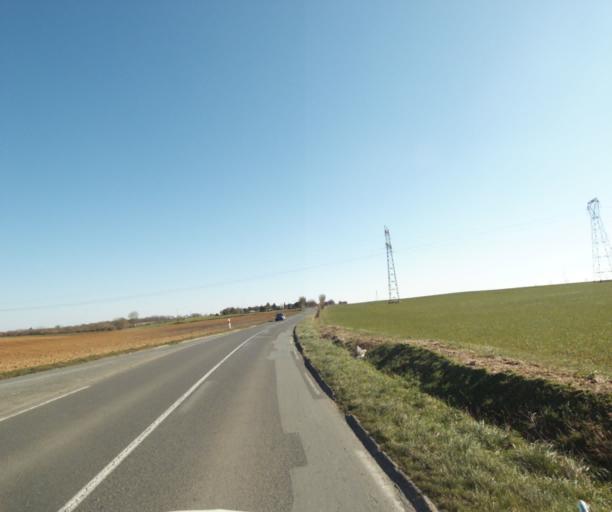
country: FR
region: Poitou-Charentes
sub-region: Departement des Deux-Sevres
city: Saint-Maxire
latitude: 46.3624
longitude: -0.4884
